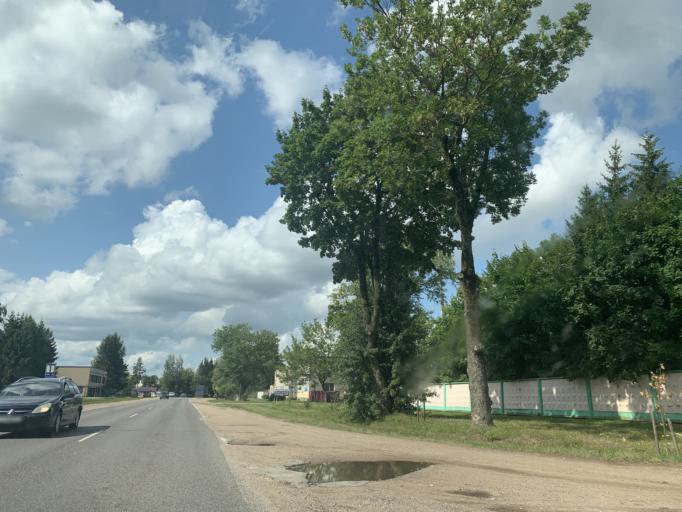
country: BY
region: Minsk
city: Enyerhyetykaw
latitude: 53.5832
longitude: 27.0539
